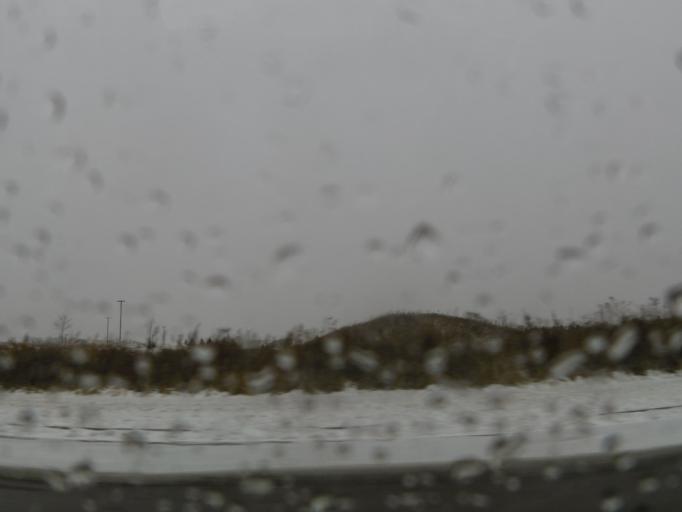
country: US
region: Minnesota
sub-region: Washington County
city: Oakdale
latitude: 44.9542
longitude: -92.9272
